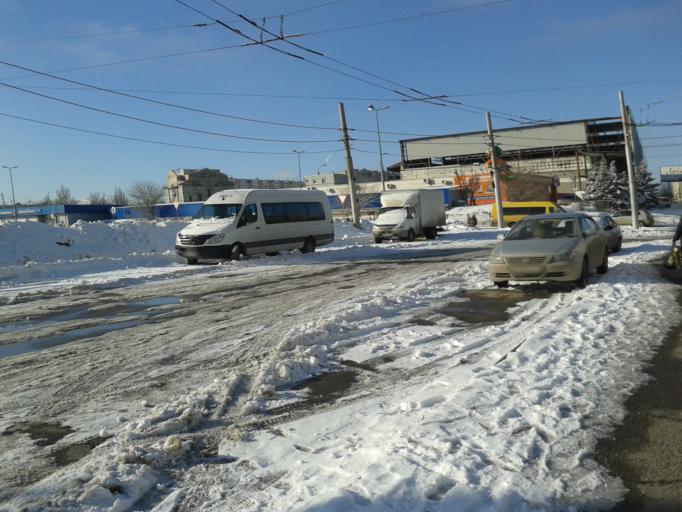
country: RU
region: Volgograd
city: Volgograd
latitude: 48.7503
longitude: 44.4975
